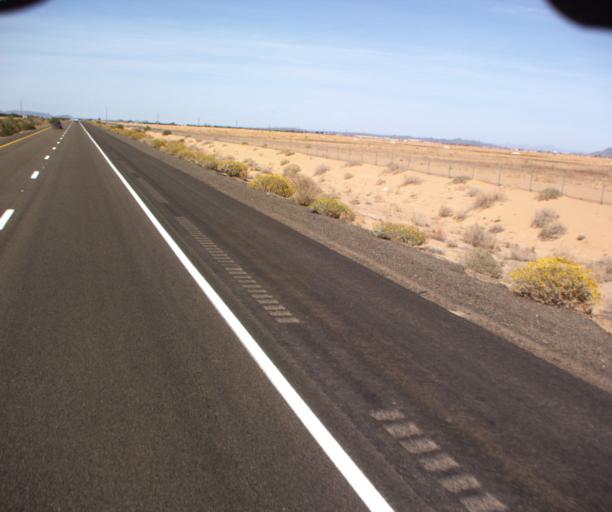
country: US
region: Arizona
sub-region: Yuma County
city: Fortuna Foothills
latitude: 32.6432
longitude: -114.5213
